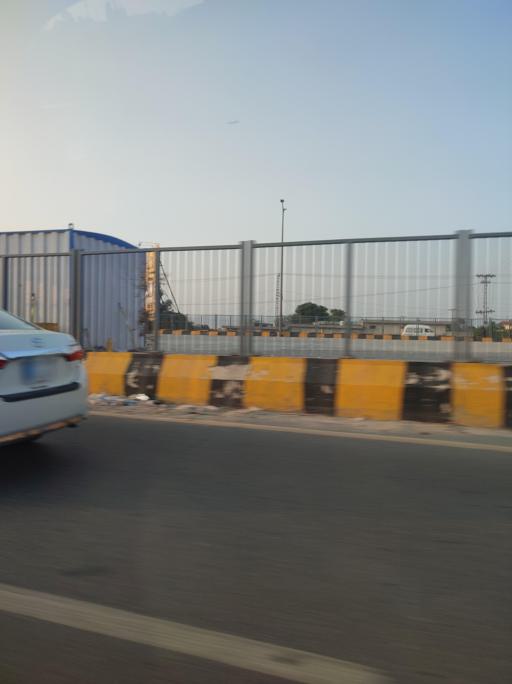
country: PK
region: Punjab
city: Rawalpindi
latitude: 33.6321
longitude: 72.9433
